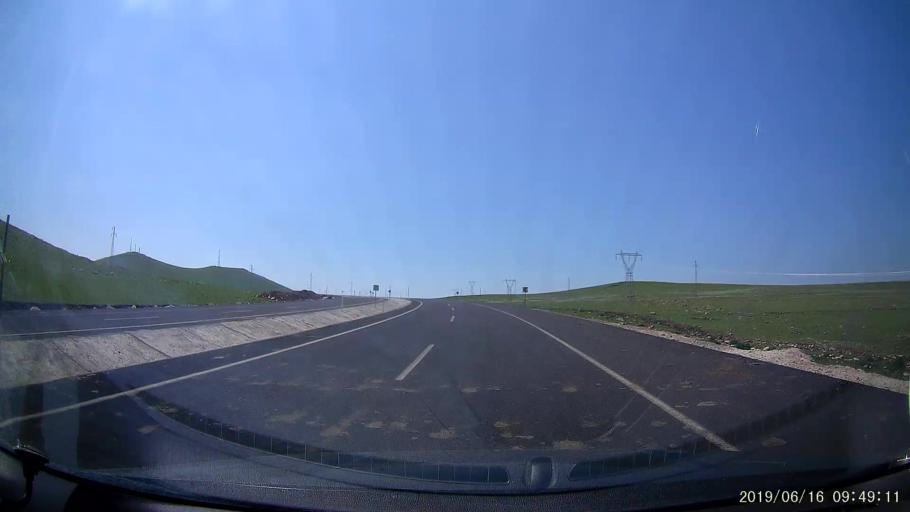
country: TR
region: Kars
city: Digor
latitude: 40.4243
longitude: 43.3565
